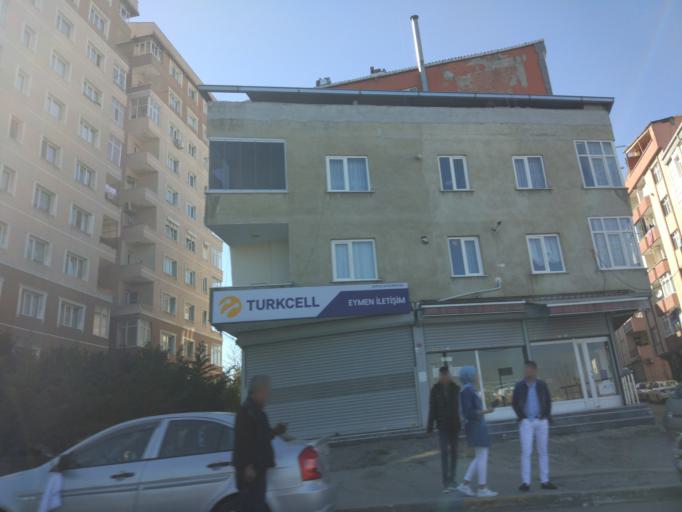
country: TR
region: Istanbul
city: Mahmutbey
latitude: 41.0181
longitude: 28.8044
